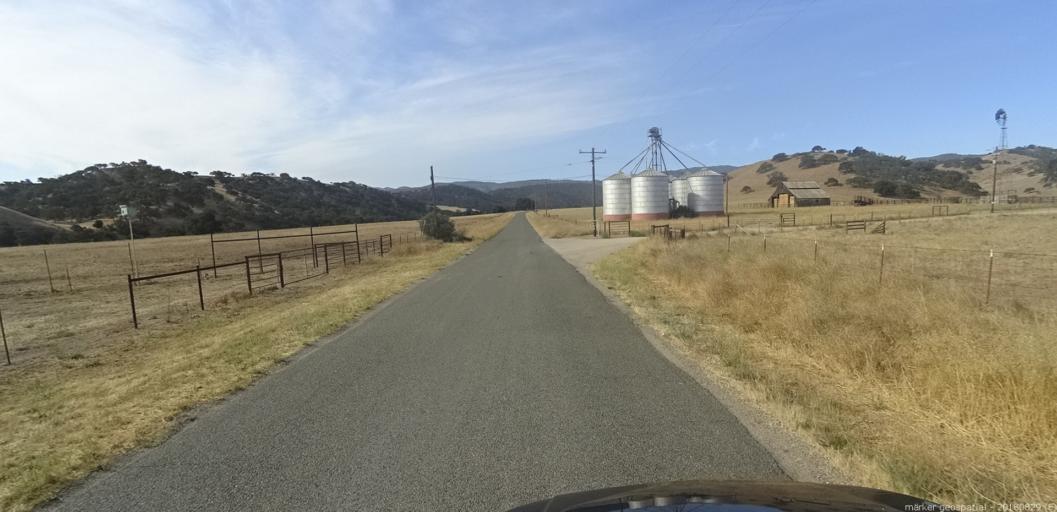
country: US
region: California
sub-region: Monterey County
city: King City
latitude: 36.0727
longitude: -121.0387
